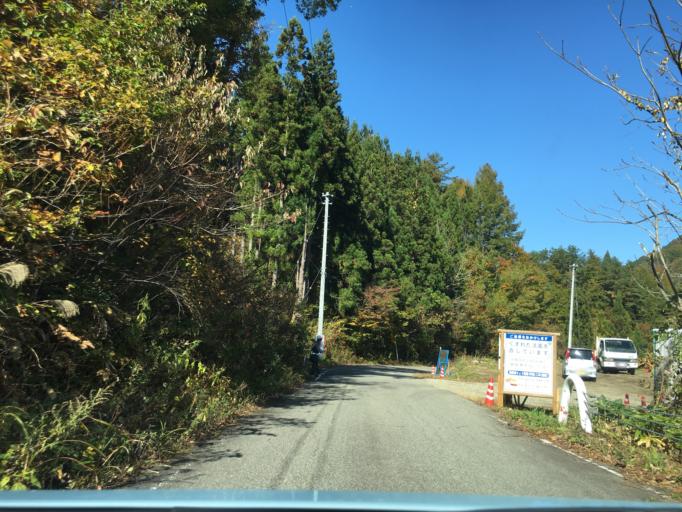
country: JP
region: Fukushima
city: Inawashiro
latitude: 37.4072
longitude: 139.9955
